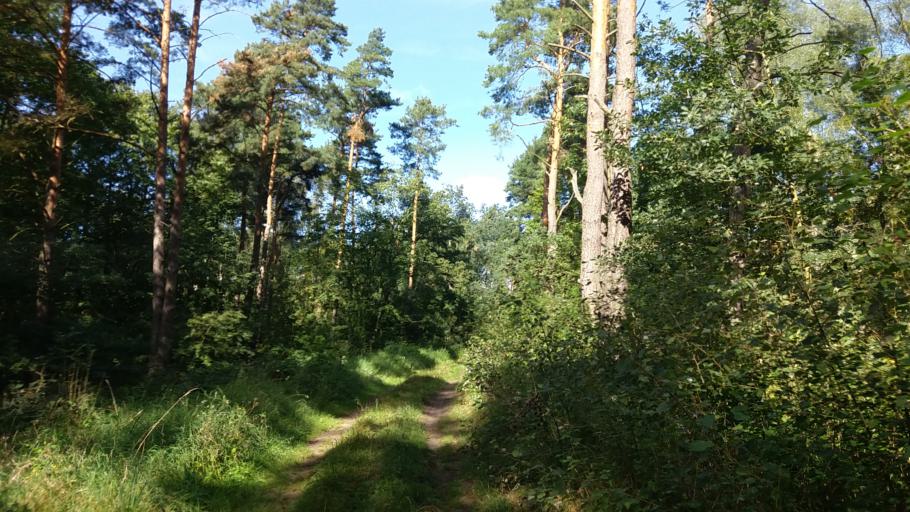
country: PL
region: West Pomeranian Voivodeship
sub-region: Powiat choszczenski
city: Krzecin
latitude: 53.1412
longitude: 15.4835
